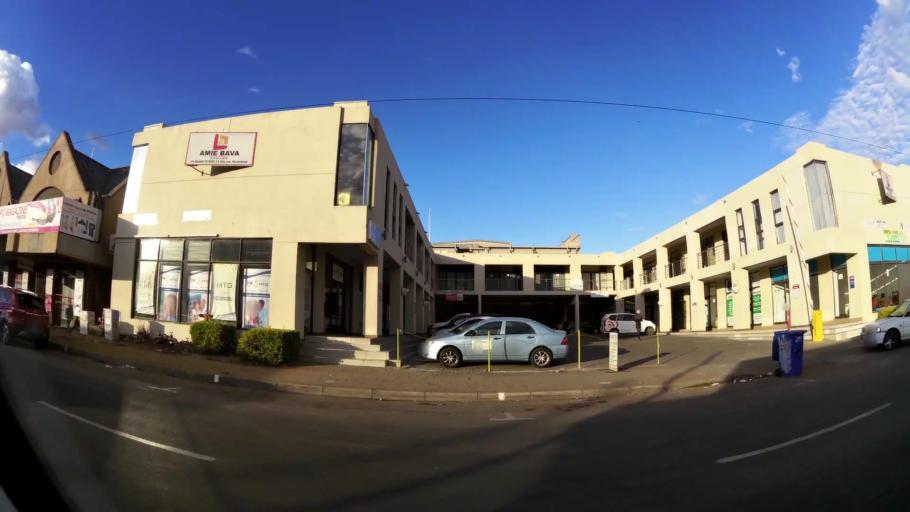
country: ZA
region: Limpopo
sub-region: Capricorn District Municipality
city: Polokwane
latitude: -23.9021
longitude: 29.4499
